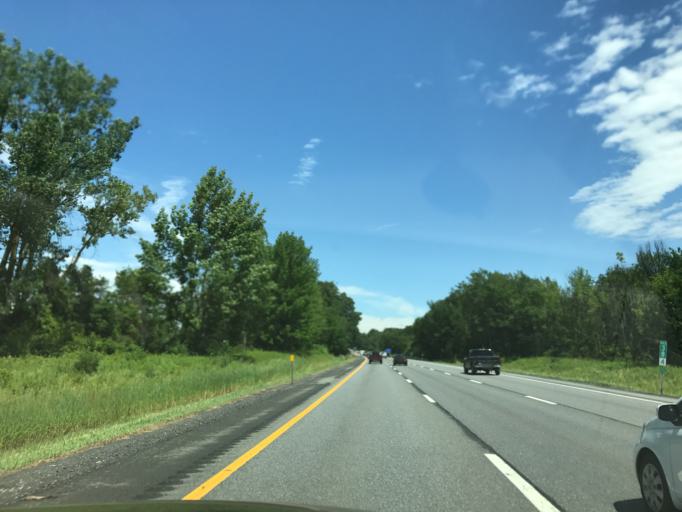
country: US
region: New York
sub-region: Warren County
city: West Glens Falls
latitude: 43.2009
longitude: -73.6973
